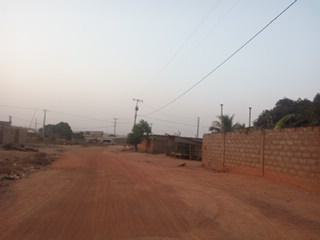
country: BJ
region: Borgou
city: Parakou
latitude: 9.3226
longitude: 2.5949
